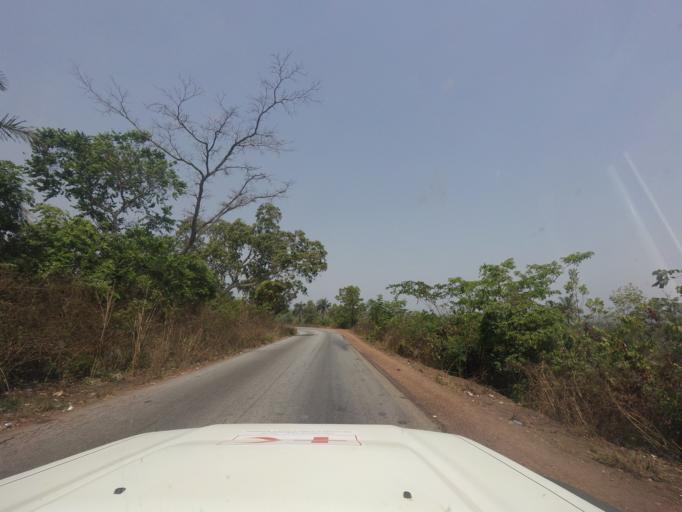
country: GN
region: Kindia
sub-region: Kindia
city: Kindia
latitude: 9.9729
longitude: -12.9332
